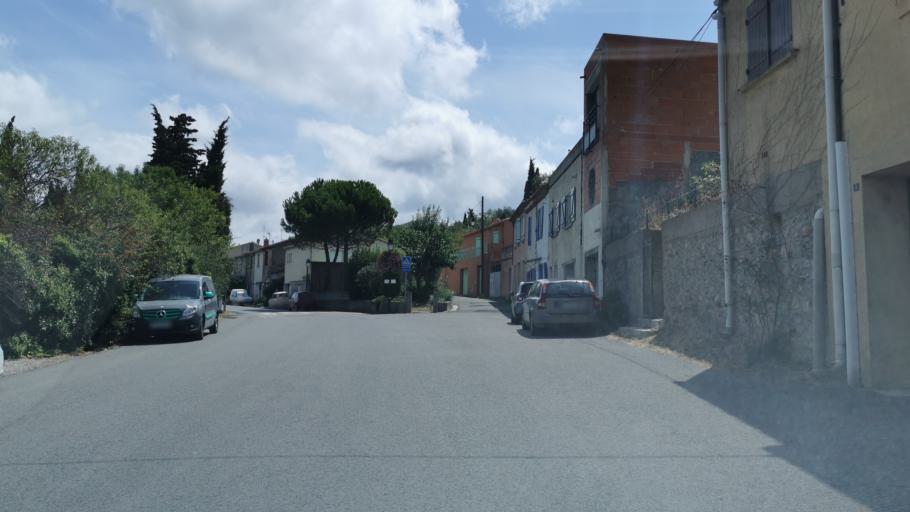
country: FR
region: Languedoc-Roussillon
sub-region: Departement de l'Aude
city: Bizanet
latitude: 43.1671
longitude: 2.8735
